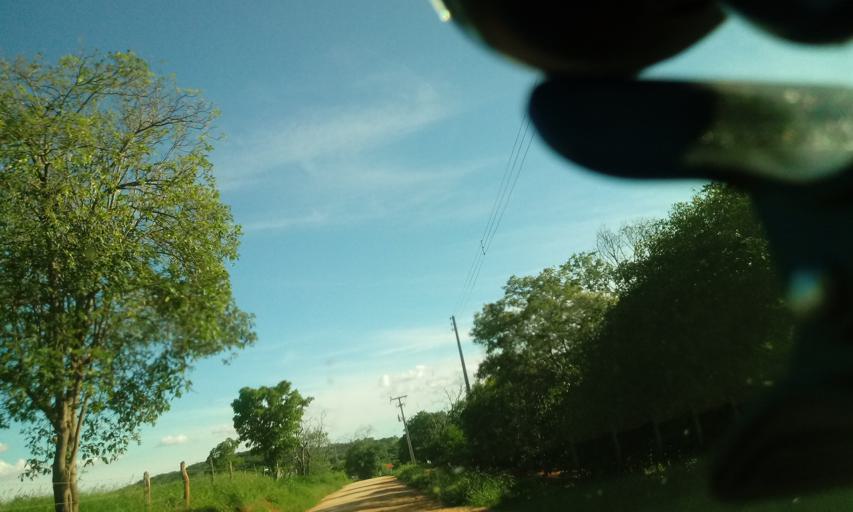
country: BR
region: Bahia
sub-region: Riacho De Santana
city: Riacho de Santana
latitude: -13.8430
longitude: -42.7672
